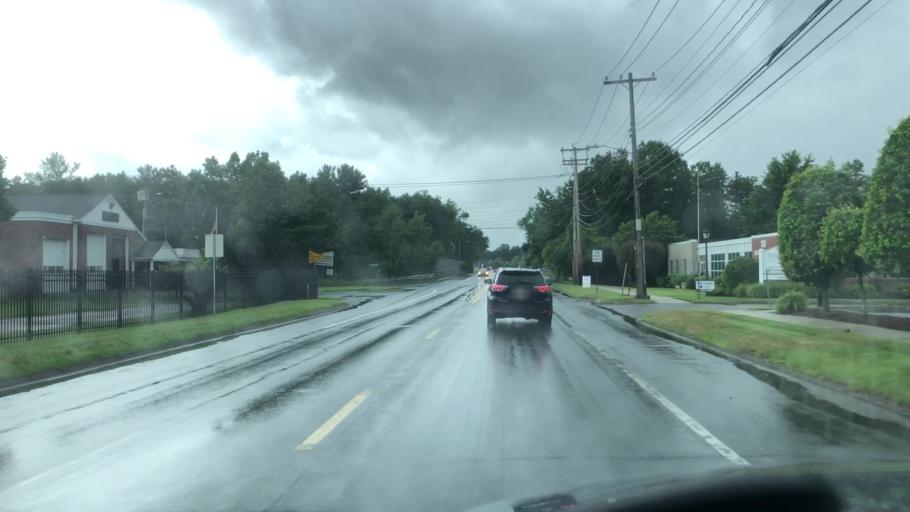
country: US
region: Massachusetts
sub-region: Hampden County
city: Westfield
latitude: 42.1455
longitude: -72.7307
